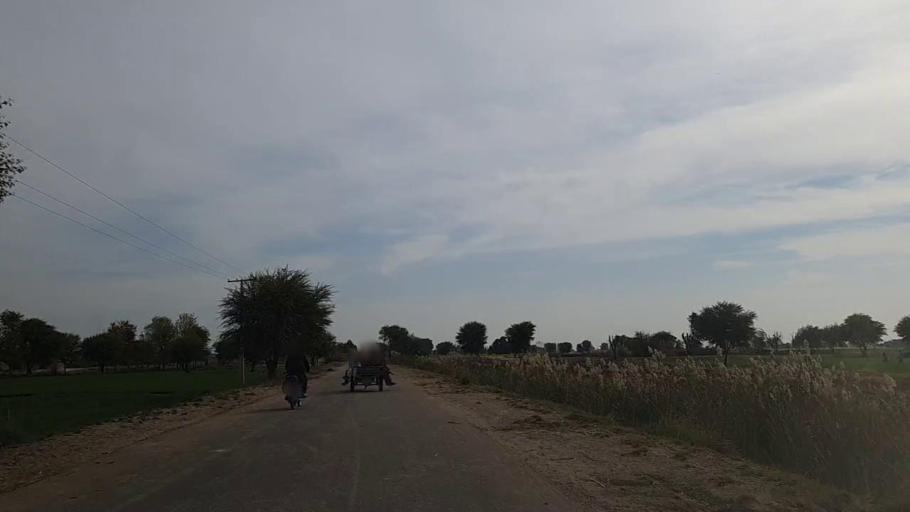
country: PK
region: Sindh
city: Daur
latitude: 26.4184
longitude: 68.4874
